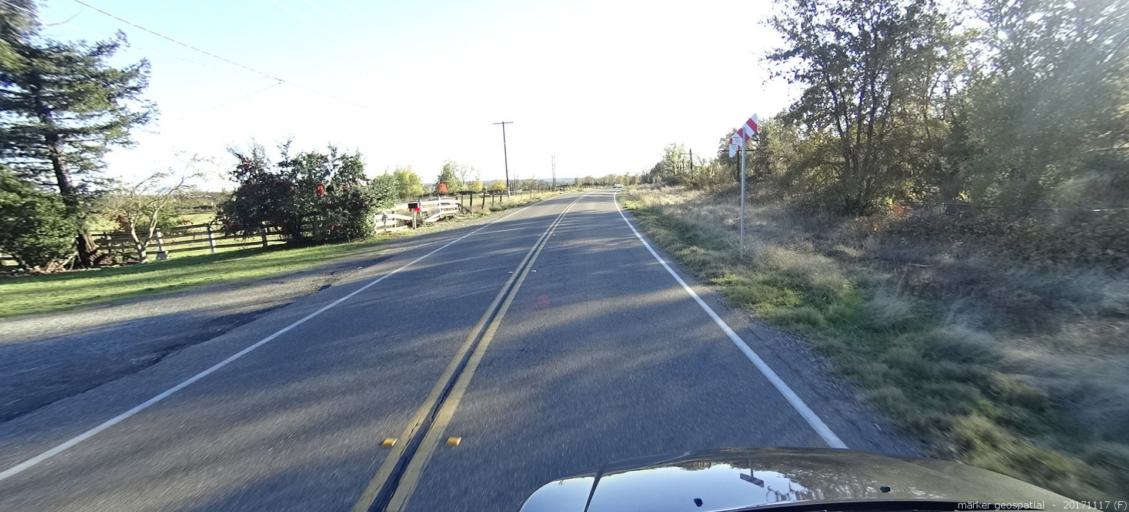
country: US
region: California
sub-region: Shasta County
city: Cottonwood
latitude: 40.4056
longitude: -122.2442
